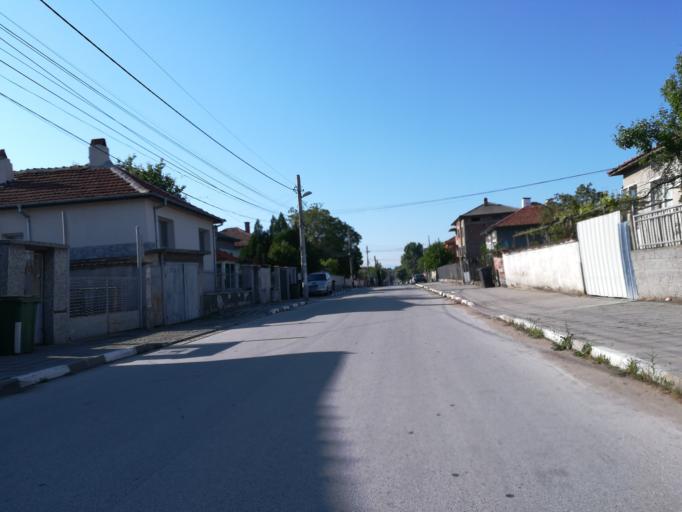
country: BG
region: Stara Zagora
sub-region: Obshtina Chirpan
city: Chirpan
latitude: 42.1073
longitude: 25.2240
